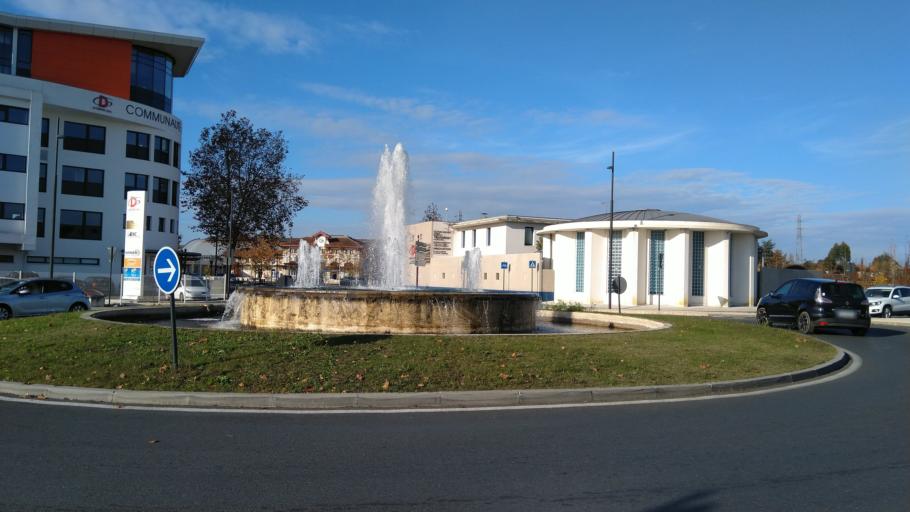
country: FR
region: Aquitaine
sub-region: Departement des Landes
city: Saint-Paul-les-Dax
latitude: 43.7189
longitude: -1.0493
